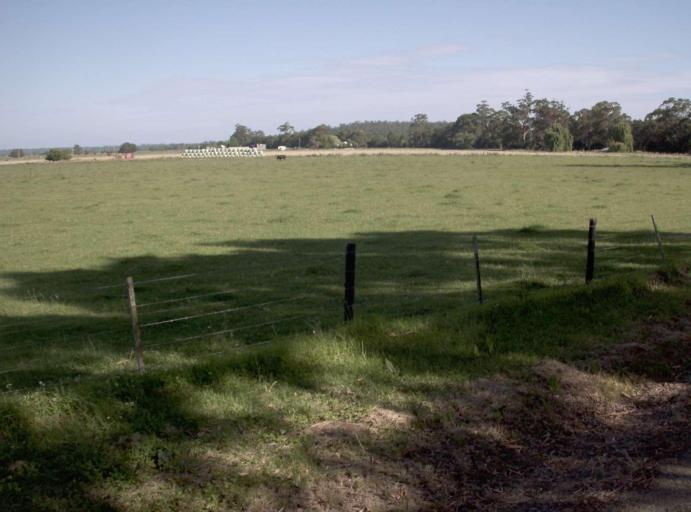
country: AU
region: Victoria
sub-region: East Gippsland
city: Lakes Entrance
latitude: -37.7356
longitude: 148.5048
